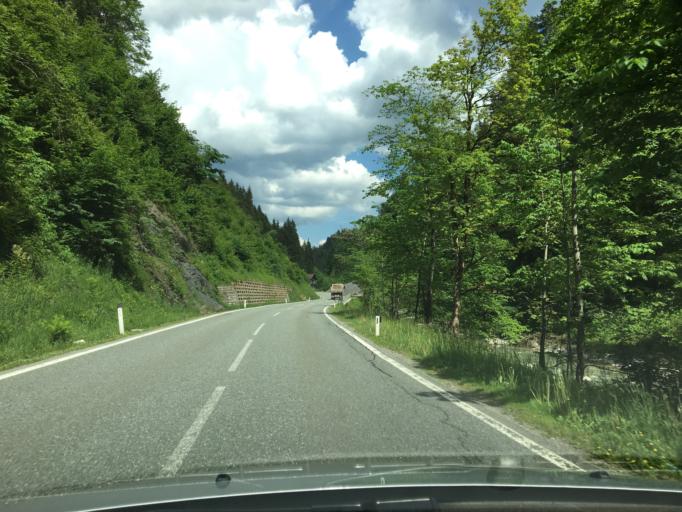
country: AT
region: Salzburg
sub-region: Politischer Bezirk Sankt Johann im Pongau
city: Wagrain
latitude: 47.3336
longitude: 13.2528
